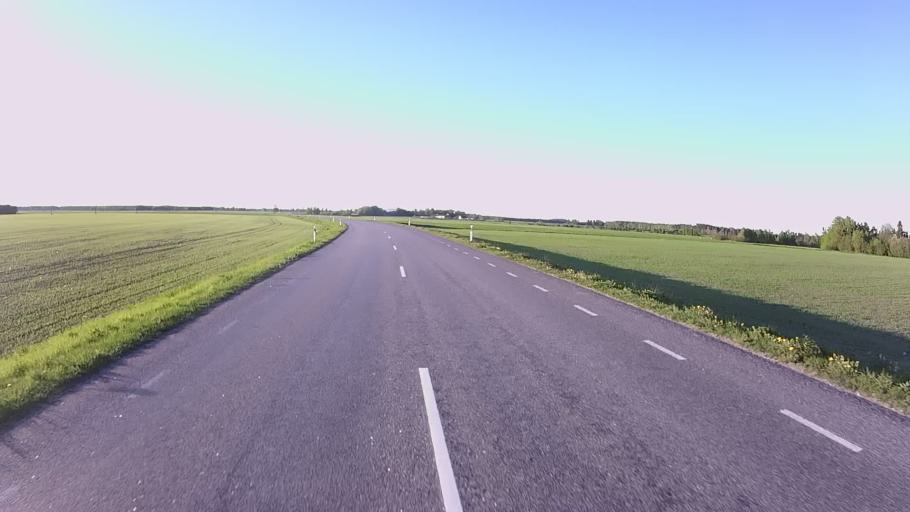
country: EE
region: Tartu
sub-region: Puhja vald
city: Puhja
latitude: 58.3100
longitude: 26.1862
